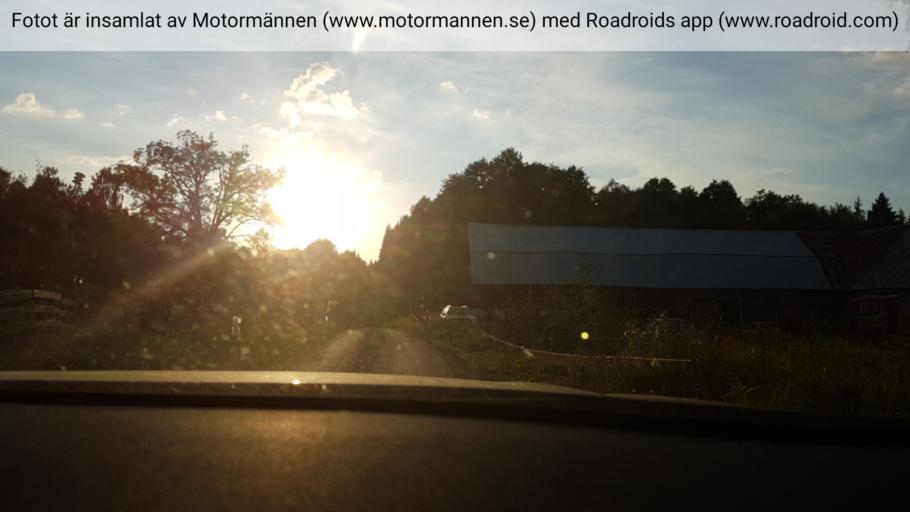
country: SE
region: Vaestra Goetaland
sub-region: Falkopings Kommun
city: Floby
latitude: 57.9745
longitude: 13.3575
